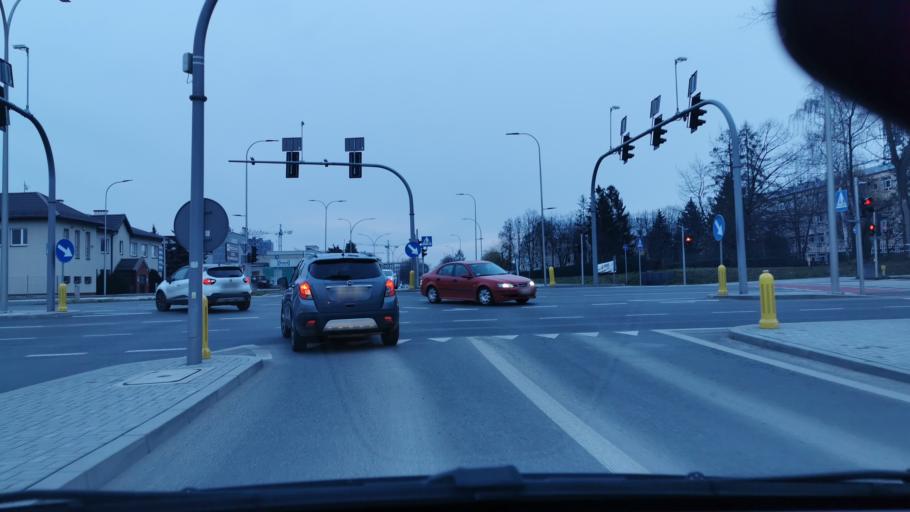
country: PL
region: Lublin Voivodeship
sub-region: Powiat lubelski
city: Lublin
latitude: 51.2471
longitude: 22.5066
